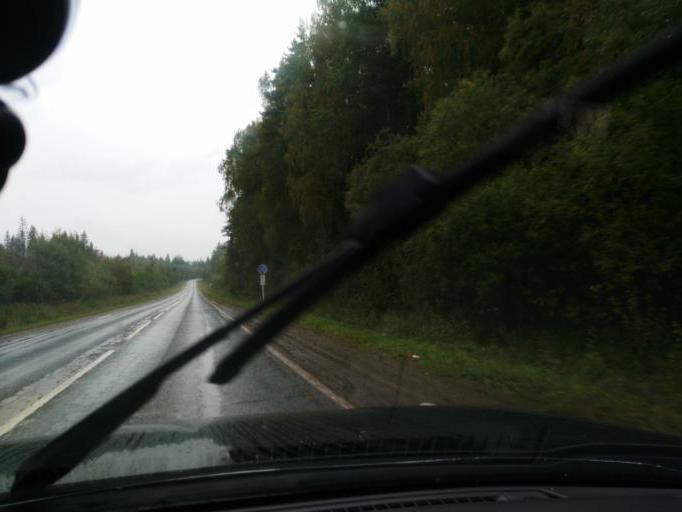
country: RU
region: Perm
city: Yugo-Kamskiy
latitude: 57.5213
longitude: 55.6850
